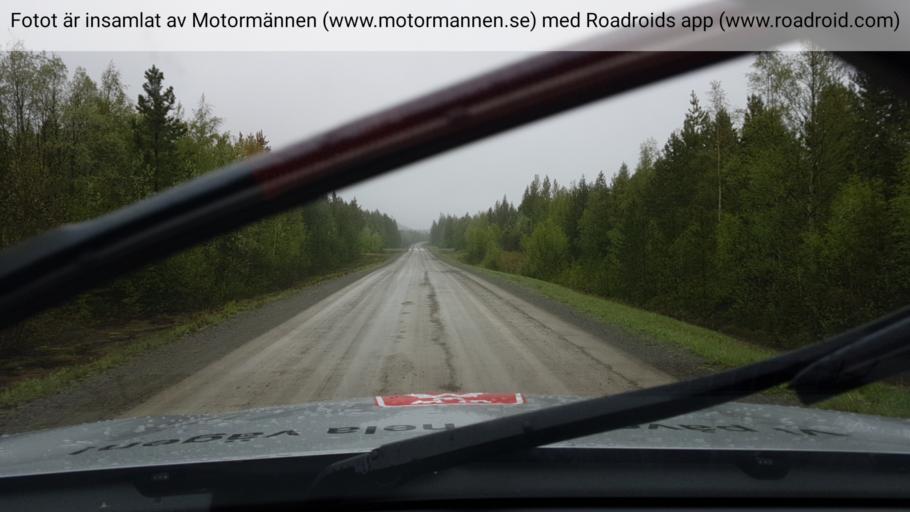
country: SE
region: Jaemtland
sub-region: Krokoms Kommun
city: Valla
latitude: 63.0602
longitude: 13.9618
